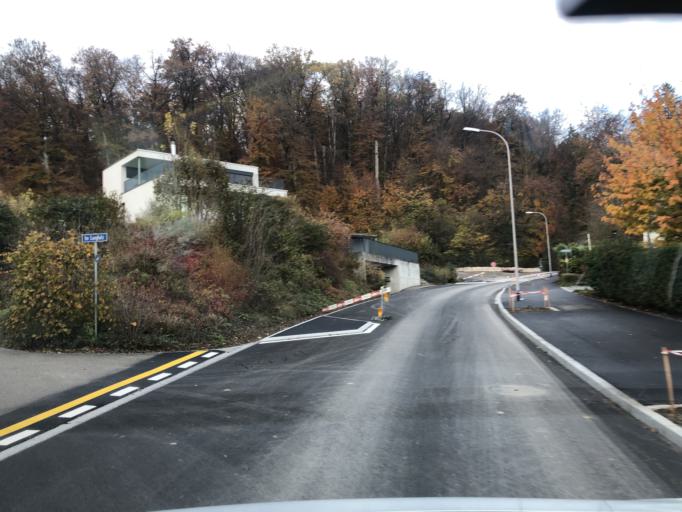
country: CH
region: Aargau
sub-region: Bezirk Baden
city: Birmenstorf
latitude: 47.4618
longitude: 8.2781
